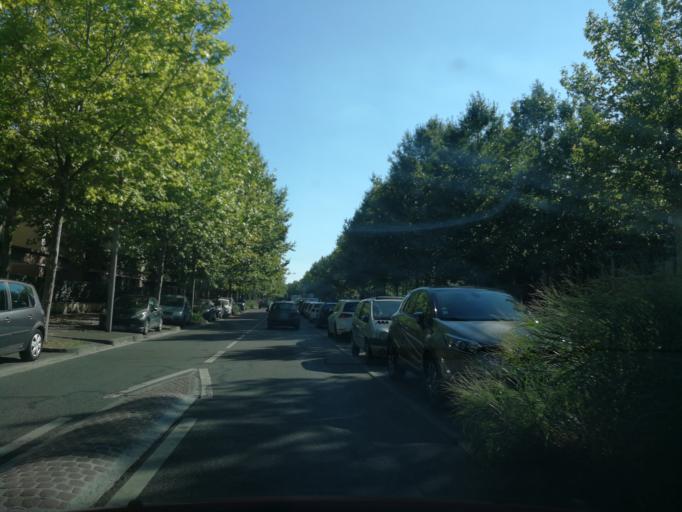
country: FR
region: Midi-Pyrenees
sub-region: Departement de la Haute-Garonne
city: Toulouse
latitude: 43.6346
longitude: 1.4521
